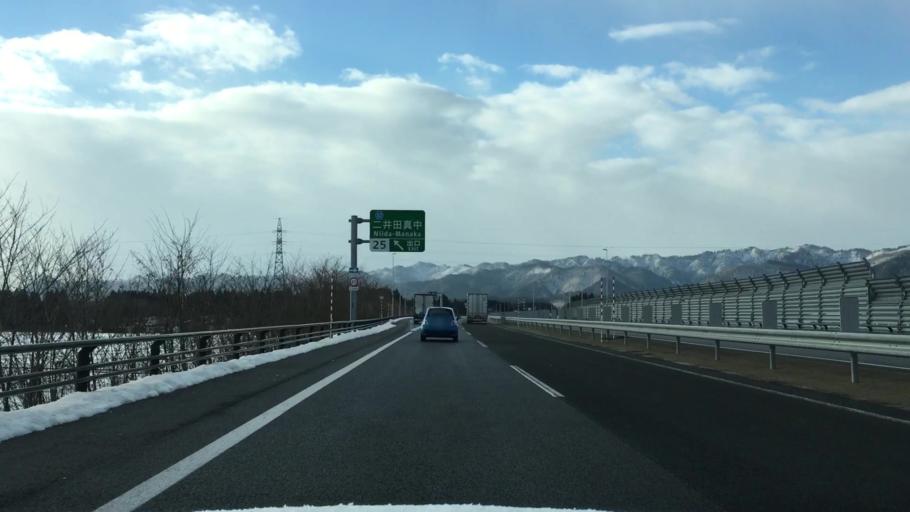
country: JP
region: Akita
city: Odate
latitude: 40.2540
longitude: 140.5189
